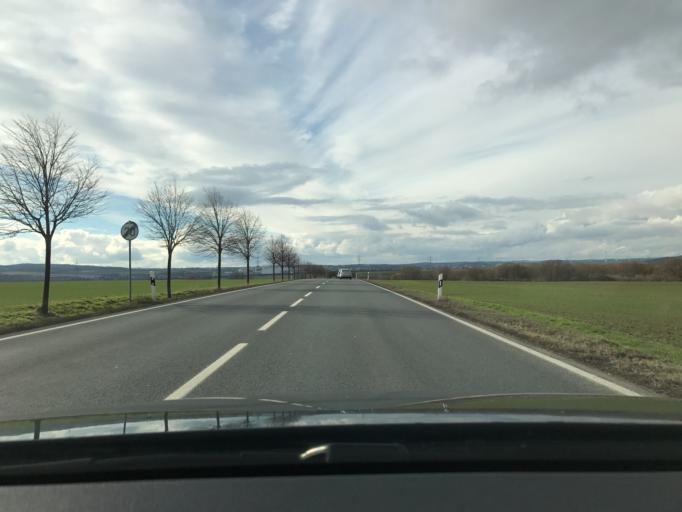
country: DE
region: Saxony-Anhalt
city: Erdeborn
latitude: 51.4999
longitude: 11.6223
